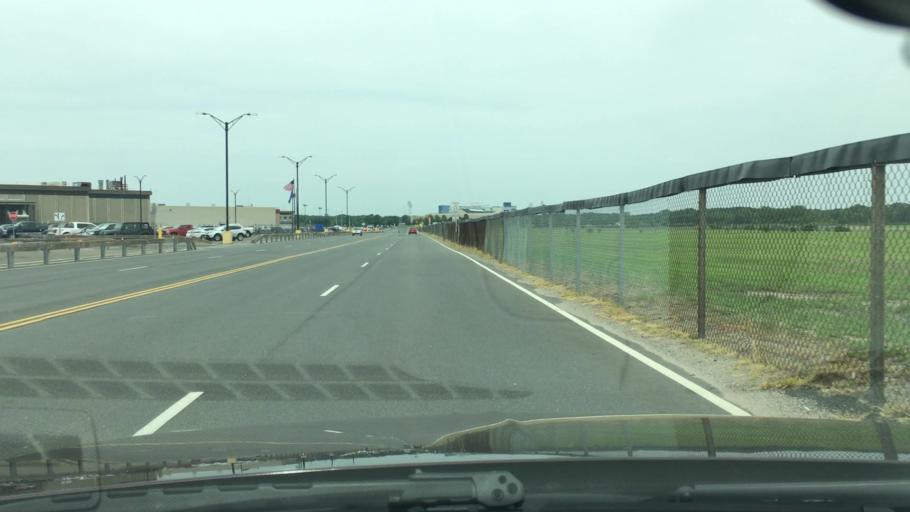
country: US
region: Connecticut
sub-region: Hartford County
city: East Hartford
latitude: 41.7484
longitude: -72.6286
